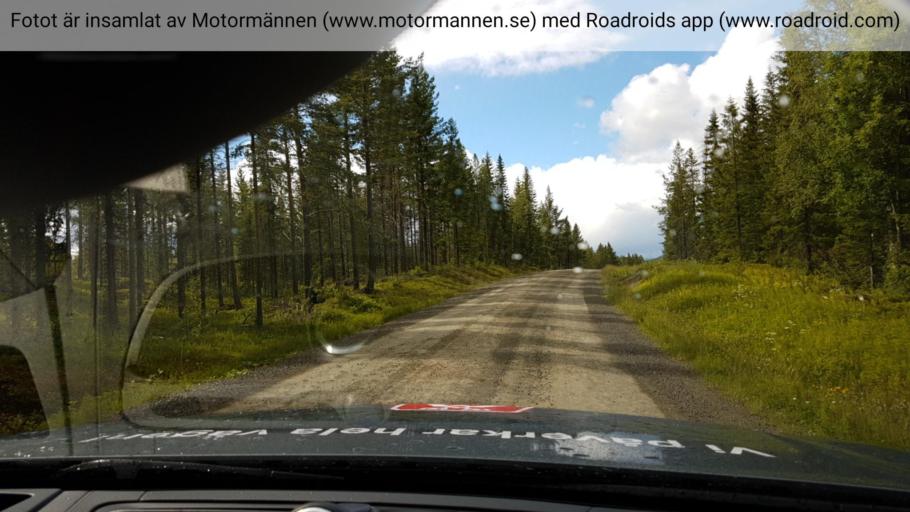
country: SE
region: Jaemtland
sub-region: Bergs Kommun
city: Hoverberg
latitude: 63.0127
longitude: 14.1031
